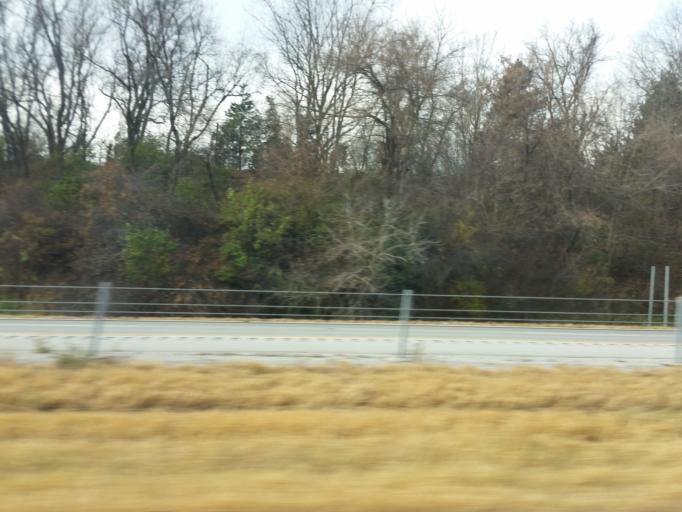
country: US
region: Illinois
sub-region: Rock Island County
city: Moline
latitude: 41.4791
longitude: -90.4943
